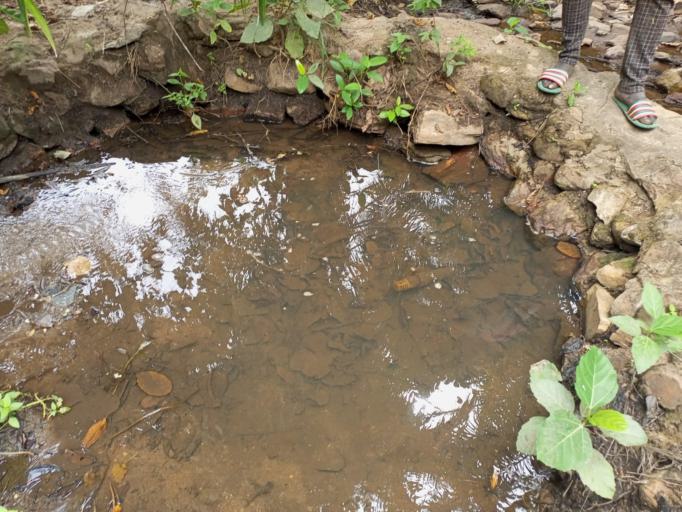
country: TG
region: Kara
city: Niamtougou
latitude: 9.6561
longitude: 0.9669
